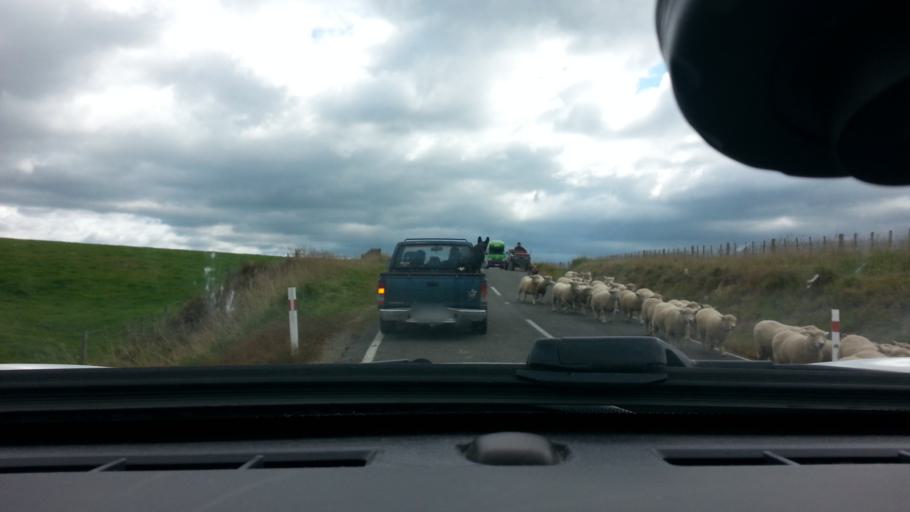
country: NZ
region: Wellington
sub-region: Upper Hutt City
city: Upper Hutt
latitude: -41.3977
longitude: 175.1766
